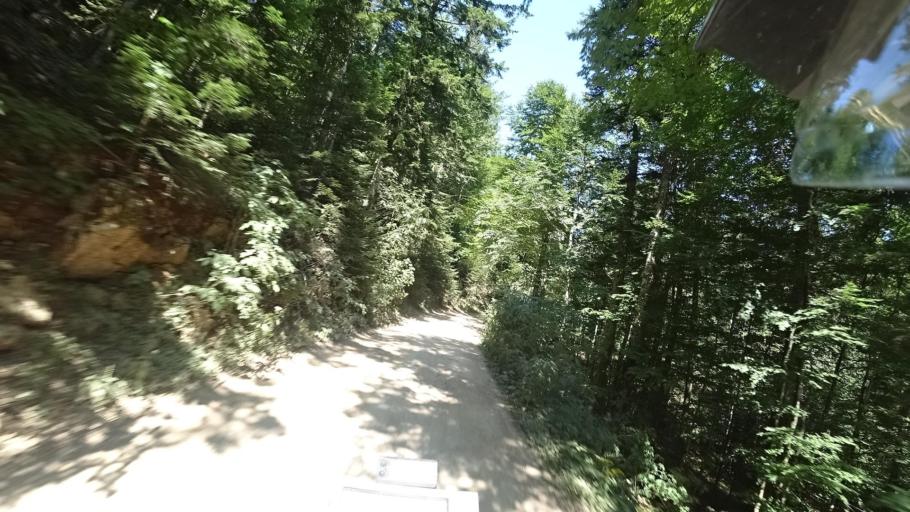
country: HR
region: Licko-Senjska
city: Popovaca
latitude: 44.5629
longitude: 15.2113
